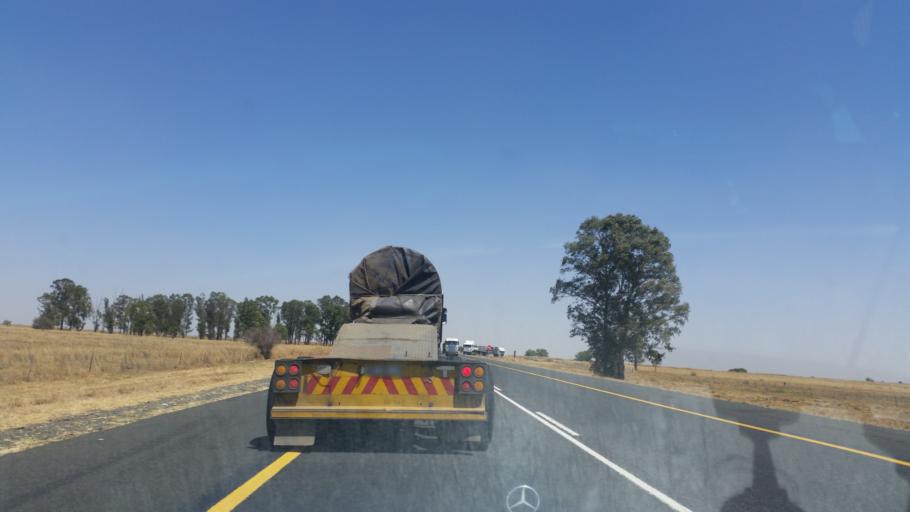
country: ZA
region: Orange Free State
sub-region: Lejweleputswa District Municipality
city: Winburg
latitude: -28.6407
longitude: 26.8901
